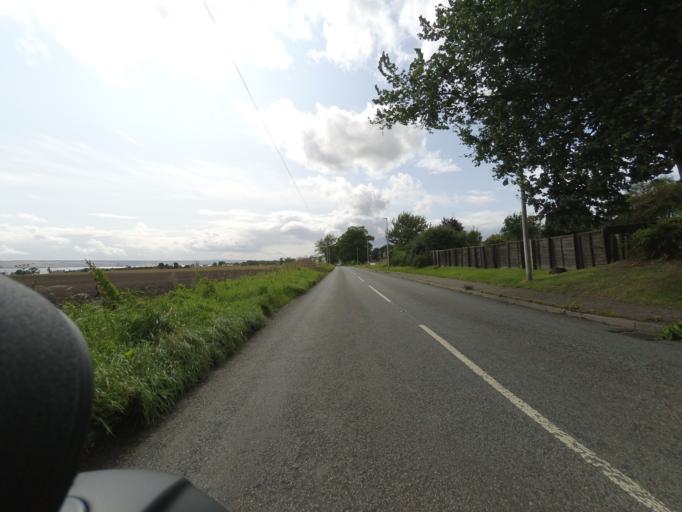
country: GB
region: Scotland
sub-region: Highland
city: Tain
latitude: 57.7307
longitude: -4.0884
